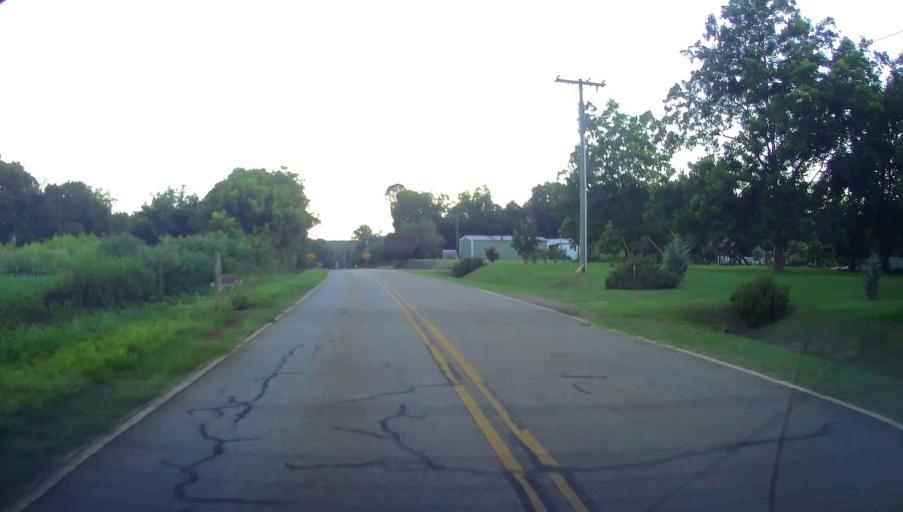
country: US
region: Georgia
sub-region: Peach County
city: Fort Valley
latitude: 32.5896
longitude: -83.8452
